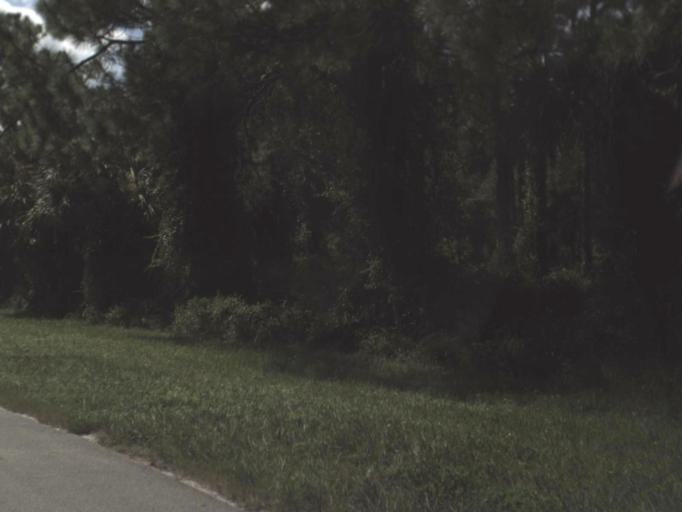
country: US
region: Florida
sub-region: Hendry County
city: LaBelle
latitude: 26.7330
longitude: -81.4377
